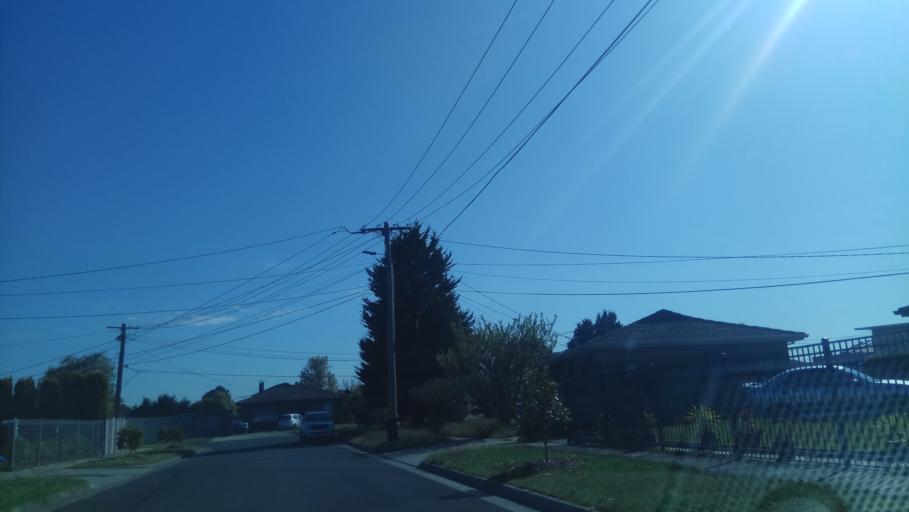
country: AU
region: Victoria
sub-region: Kingston
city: Clayton South
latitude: -37.9461
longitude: 145.1103
